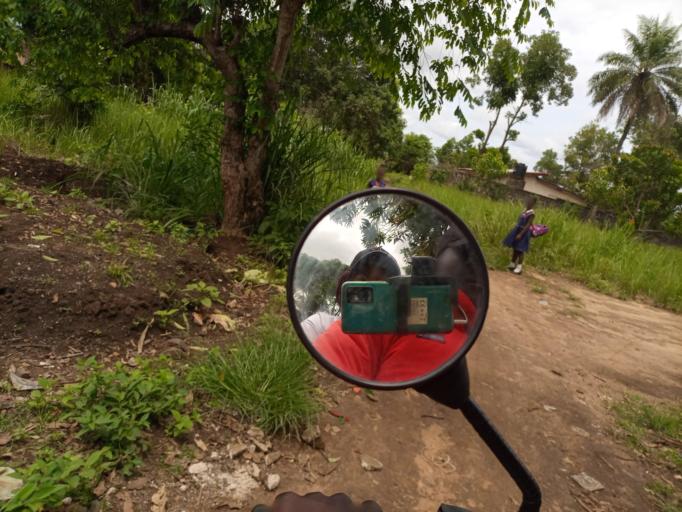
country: SL
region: Southern Province
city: Bo
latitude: 7.9679
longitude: -11.7142
